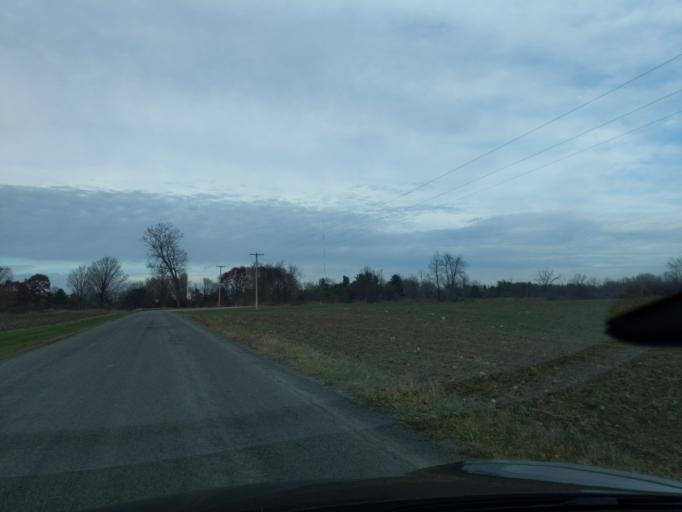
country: US
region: Michigan
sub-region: Ingham County
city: Okemos
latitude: 42.6716
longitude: -84.3834
